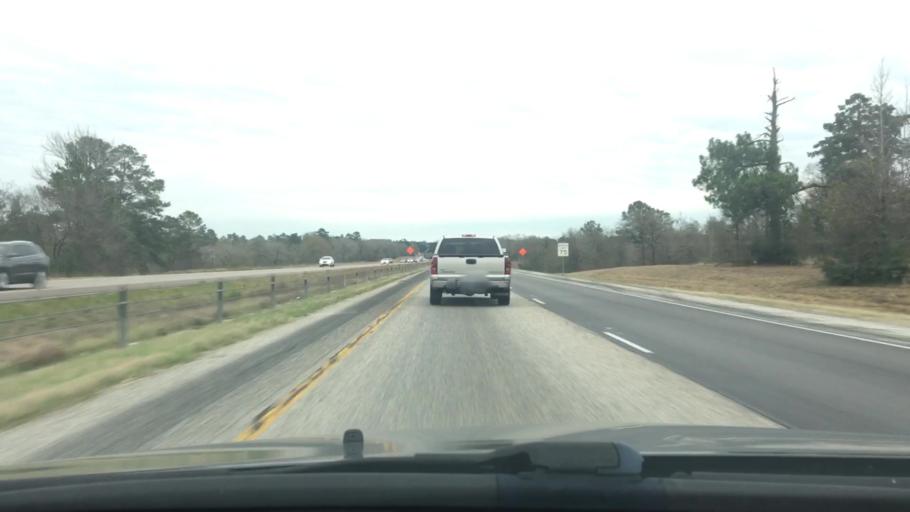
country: US
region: Texas
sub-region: Walker County
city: Huntsville
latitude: 30.7718
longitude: -95.6431
